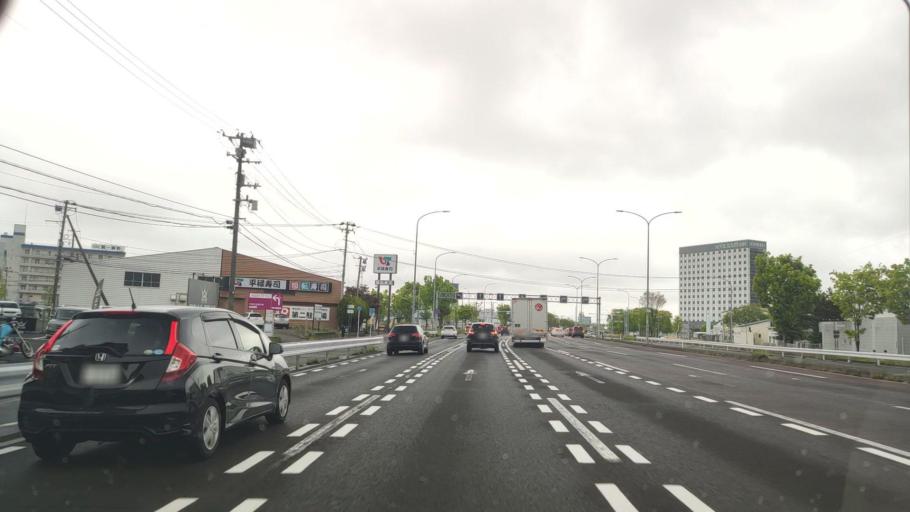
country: JP
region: Miyagi
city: Sendai-shi
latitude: 38.2496
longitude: 140.9266
